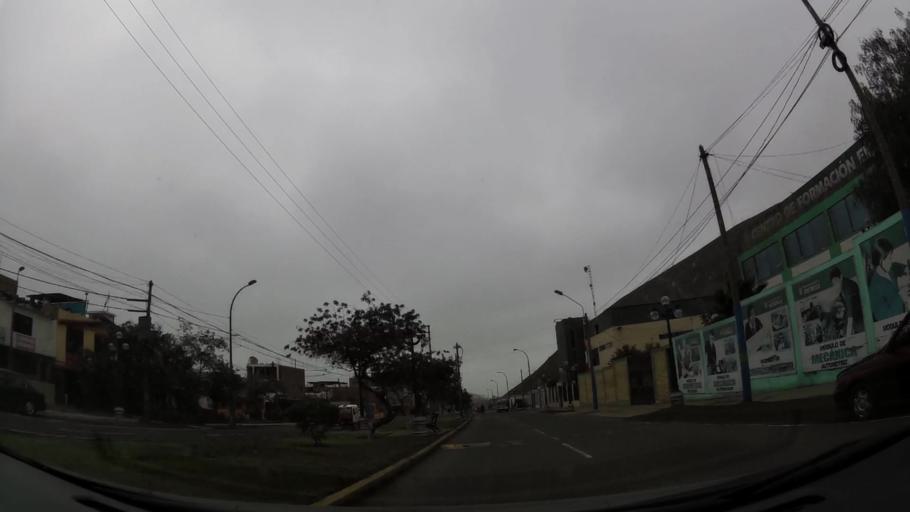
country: PE
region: Lima
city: Ventanilla
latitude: -11.8691
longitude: -77.1179
